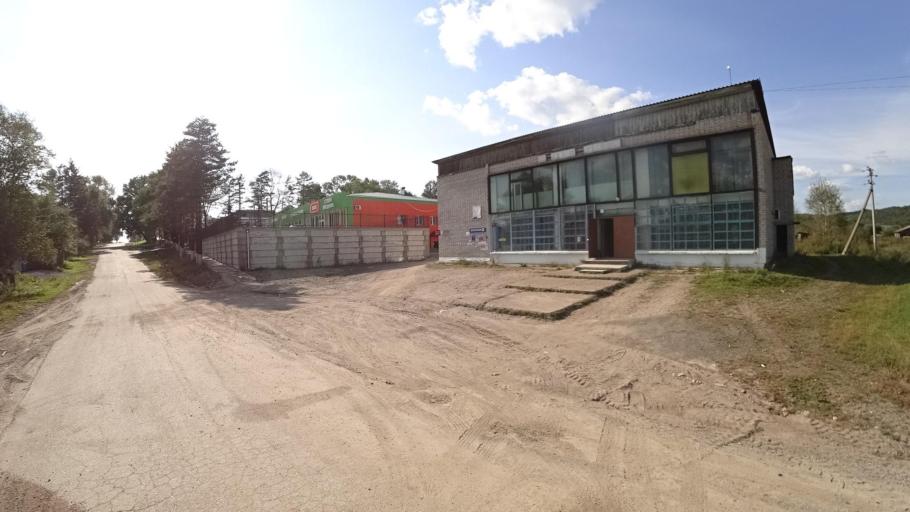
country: RU
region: Jewish Autonomous Oblast
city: Birakan
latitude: 48.9941
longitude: 131.7220
